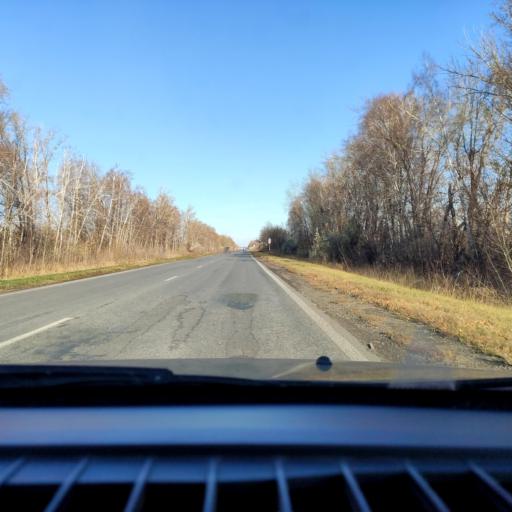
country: RU
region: Samara
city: Tol'yatti
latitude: 53.6138
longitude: 49.3141
